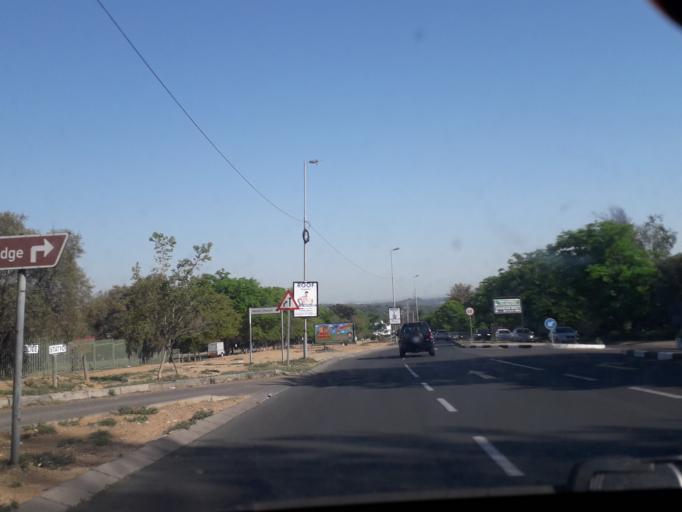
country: ZA
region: Gauteng
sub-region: City of Johannesburg Metropolitan Municipality
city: Midrand
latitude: -26.0646
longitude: 28.0742
